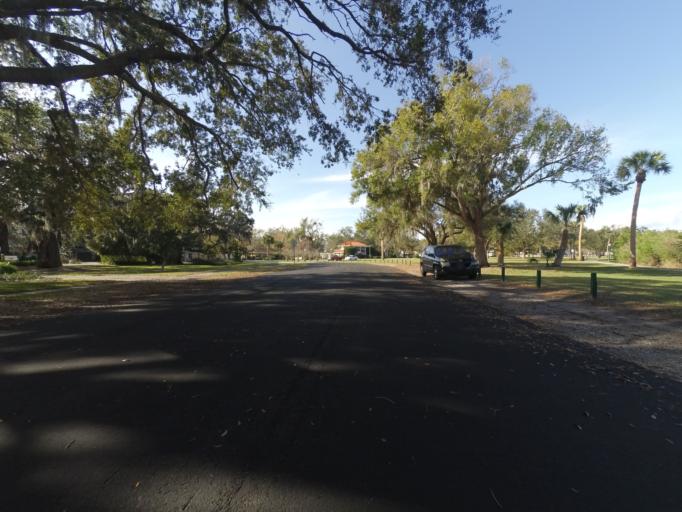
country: US
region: Florida
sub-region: Lake County
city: Mount Dora
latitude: 28.8093
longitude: -81.6640
